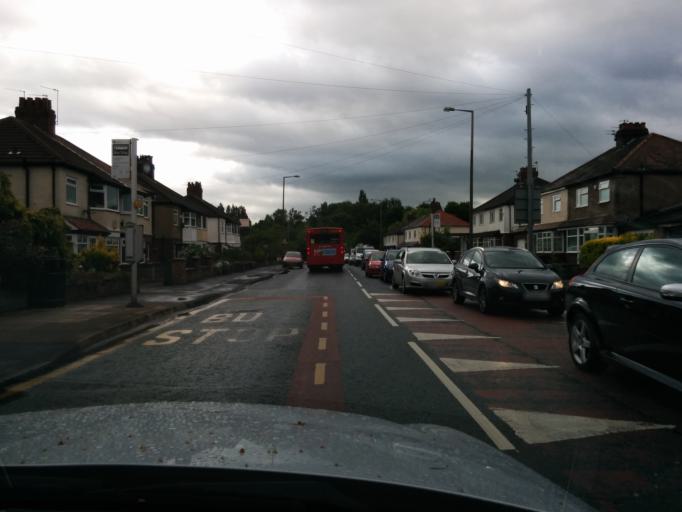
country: GB
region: England
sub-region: Borough of Stockport
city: Cheadle Hulme
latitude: 53.3802
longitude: -2.1872
